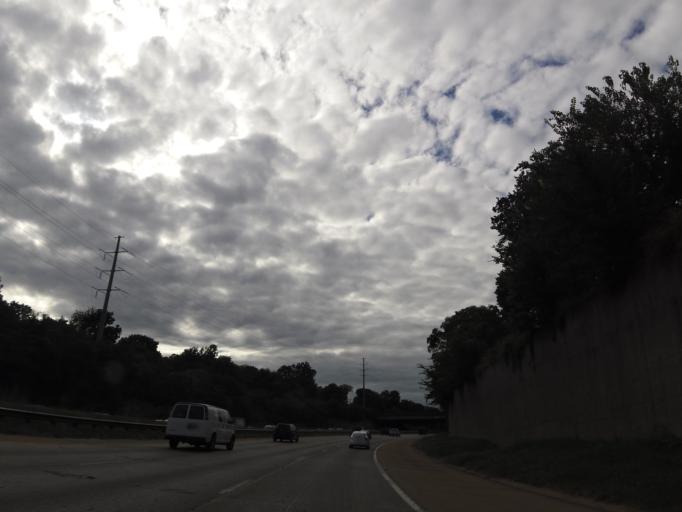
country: US
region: Tennessee
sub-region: Davidson County
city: Oak Hill
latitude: 36.1165
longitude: -86.7985
